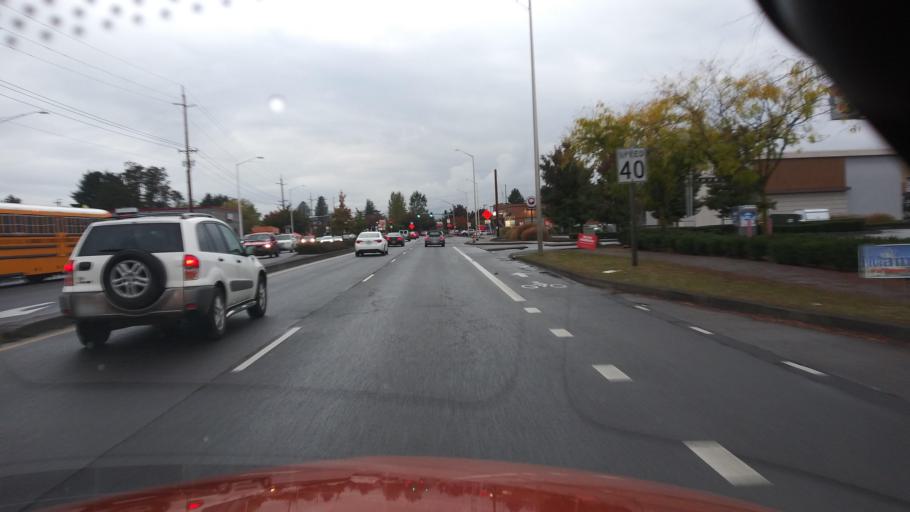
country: US
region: Oregon
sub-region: Washington County
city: Cornelius
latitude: 45.5202
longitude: -123.0445
